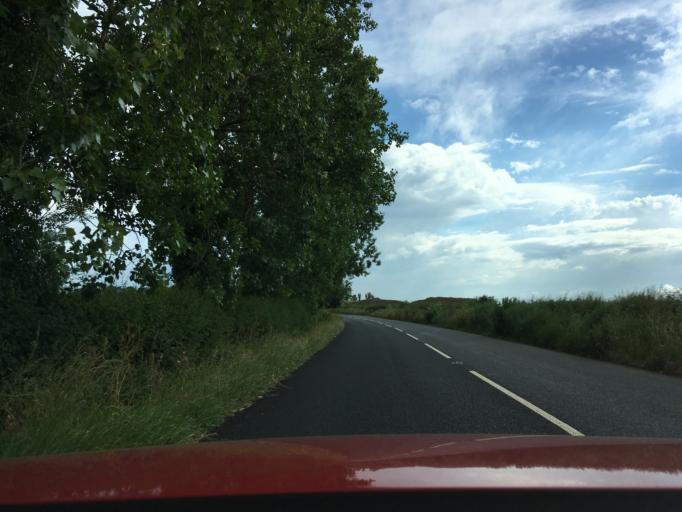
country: GB
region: England
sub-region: Gloucestershire
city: Stonehouse
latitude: 51.7900
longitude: -2.2892
